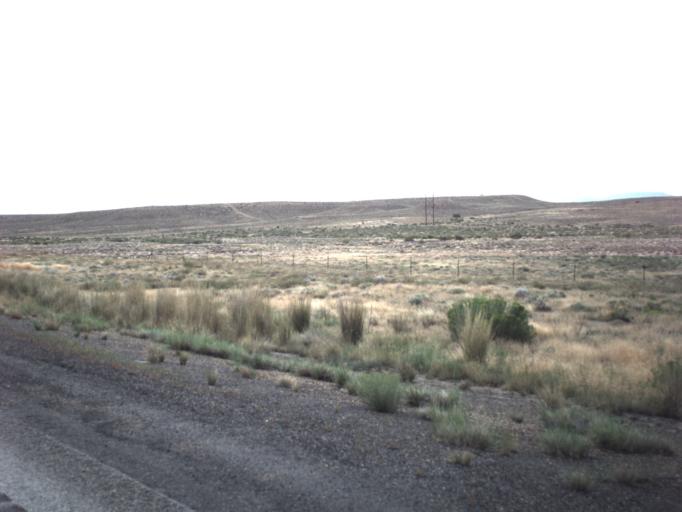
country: US
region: Utah
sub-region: Carbon County
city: Wellington
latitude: 39.5445
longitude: -110.6172
